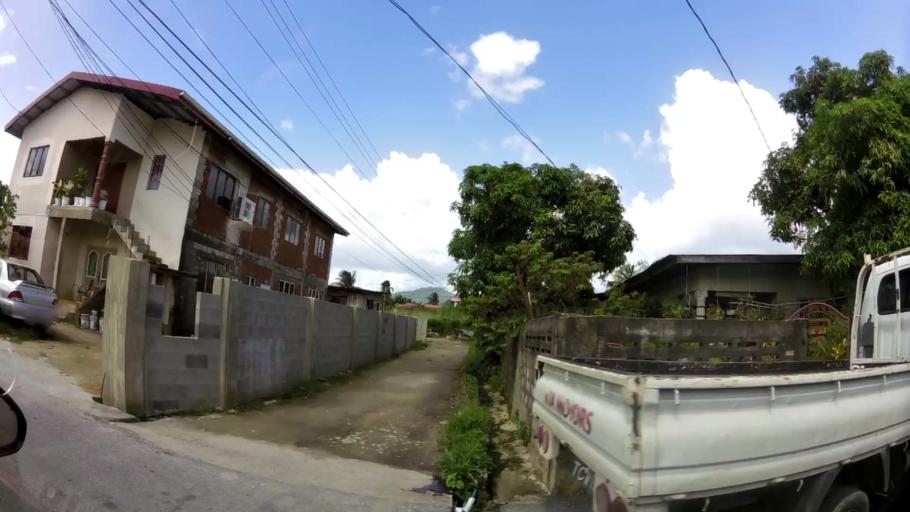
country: TT
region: Borough of Arima
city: Arima
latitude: 10.6309
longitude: -61.2807
